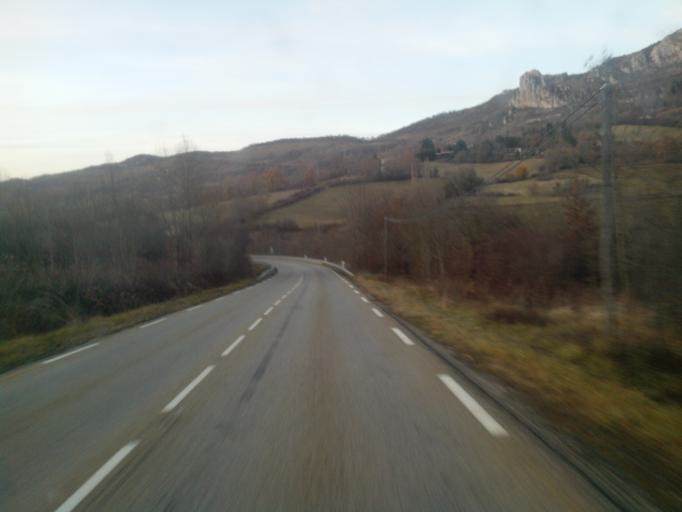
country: FR
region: Midi-Pyrenees
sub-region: Departement de l'Ariege
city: Lavelanet
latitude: 42.9221
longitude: 1.7515
